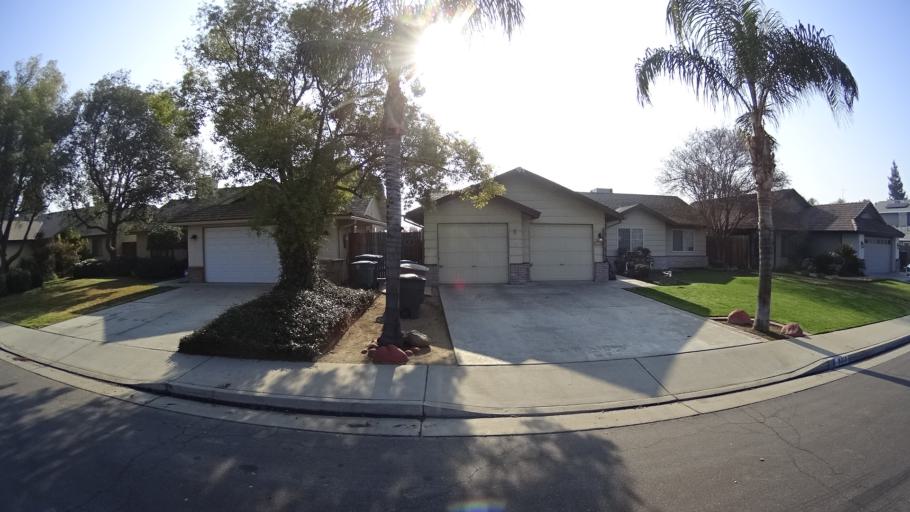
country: US
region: California
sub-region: Kern County
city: Greenacres
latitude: 35.3936
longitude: -119.1061
